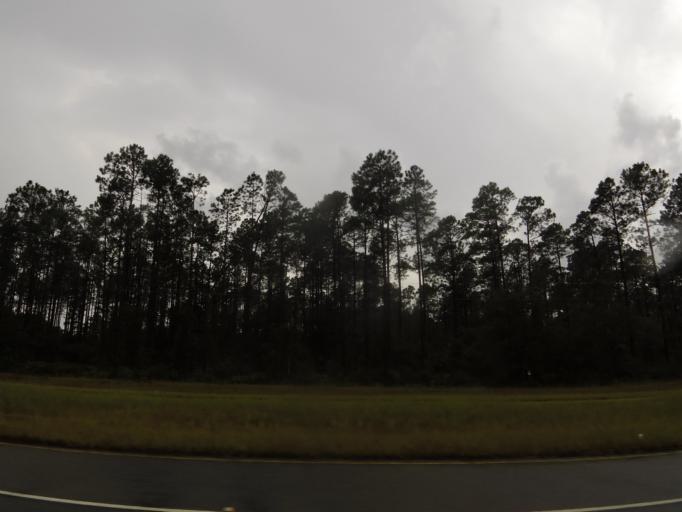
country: US
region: Georgia
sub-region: Wayne County
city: Jesup
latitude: 31.4726
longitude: -81.7231
